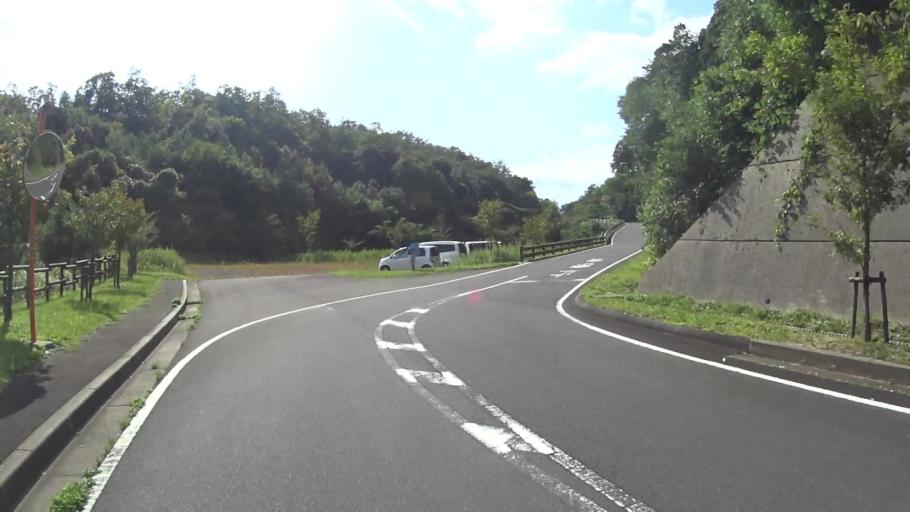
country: JP
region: Kyoto
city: Miyazu
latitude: 35.6271
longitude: 135.2351
